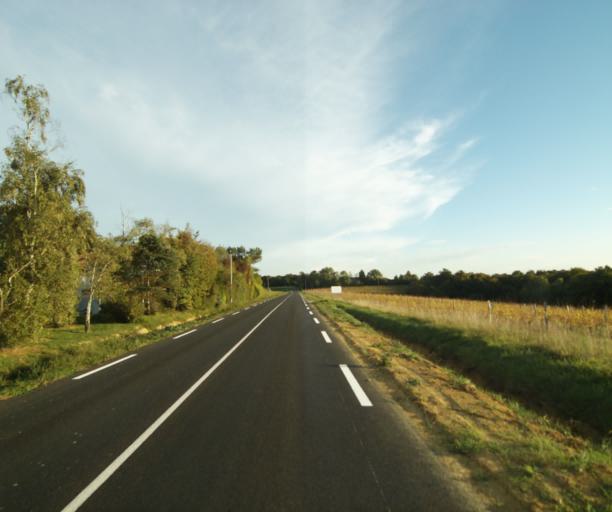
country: FR
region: Midi-Pyrenees
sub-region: Departement du Gers
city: Eauze
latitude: 43.8794
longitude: 0.0308
